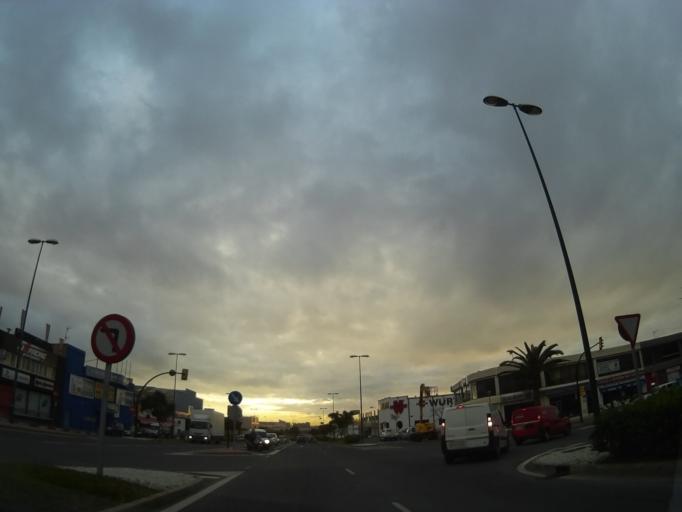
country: ES
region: Andalusia
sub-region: Provincia de Malaga
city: Malaga
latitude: 36.7074
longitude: -4.4753
